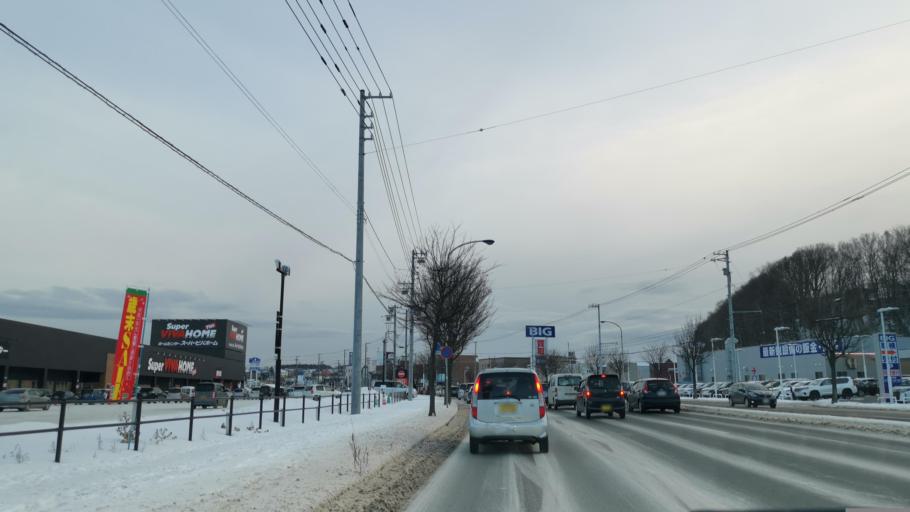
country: JP
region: Hokkaido
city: Sapporo
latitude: 42.9920
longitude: 141.4378
